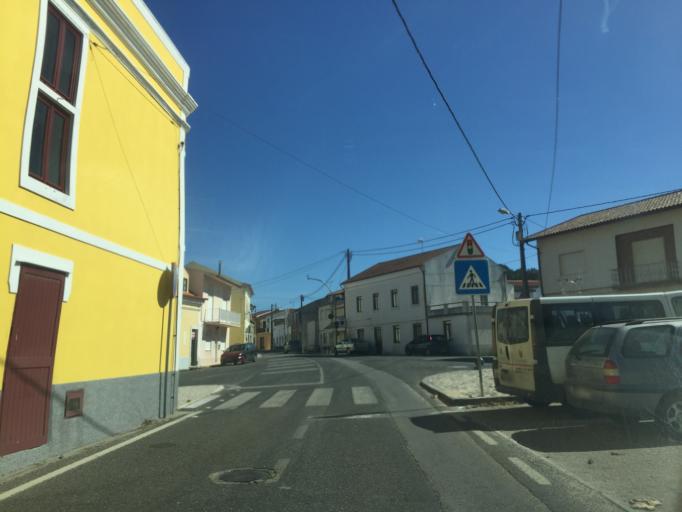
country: PT
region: Coimbra
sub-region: Figueira da Foz
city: Tavarede
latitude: 40.2146
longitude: -8.8559
